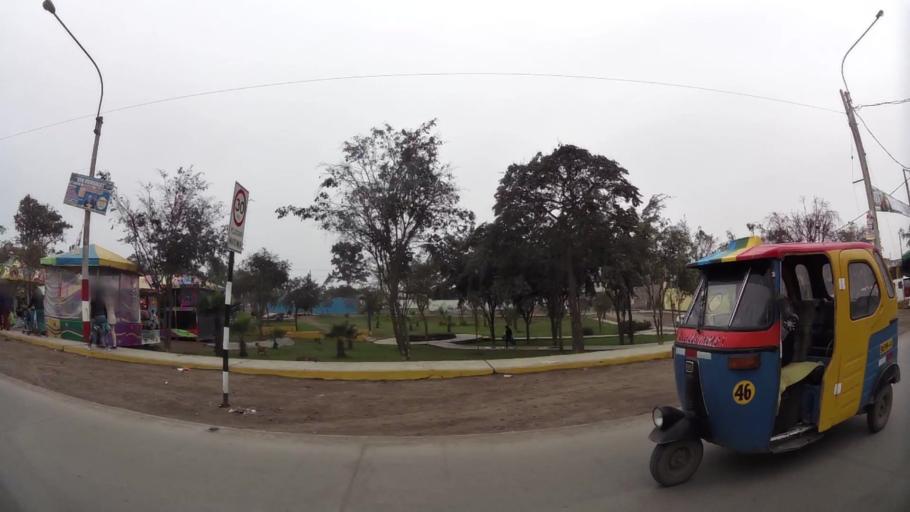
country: PE
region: Lima
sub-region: Lima
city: Surco
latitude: -12.1881
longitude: -76.9260
